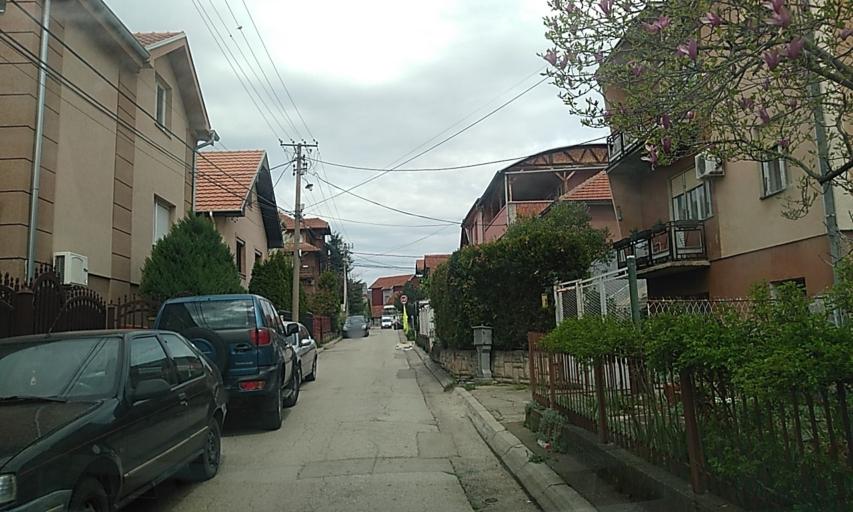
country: RS
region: Central Serbia
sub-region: Nisavski Okrug
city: Nis
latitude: 43.3359
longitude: 21.9148
